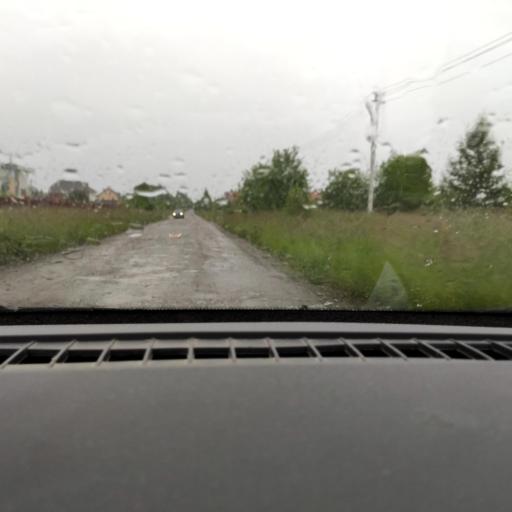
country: RU
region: Perm
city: Perm
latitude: 58.0396
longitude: 56.3725
